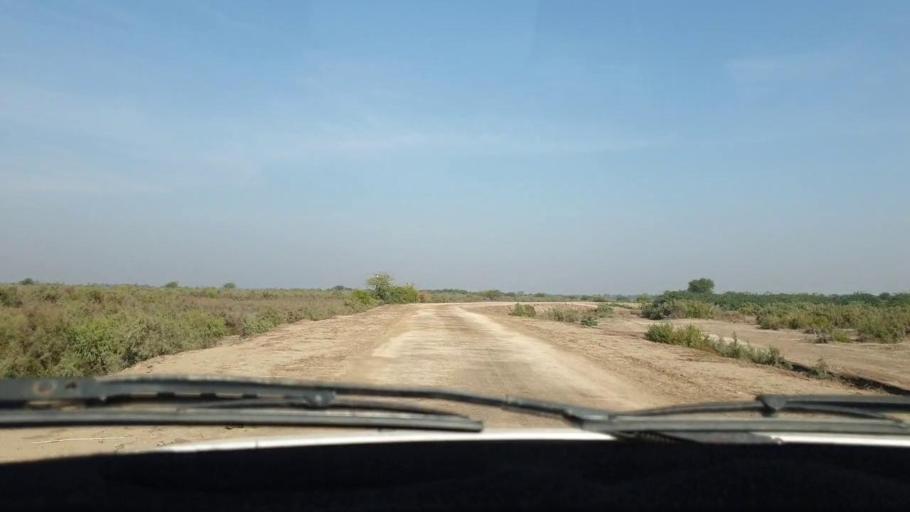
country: PK
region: Sindh
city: Tando Muhammad Khan
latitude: 24.9859
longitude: 68.4621
